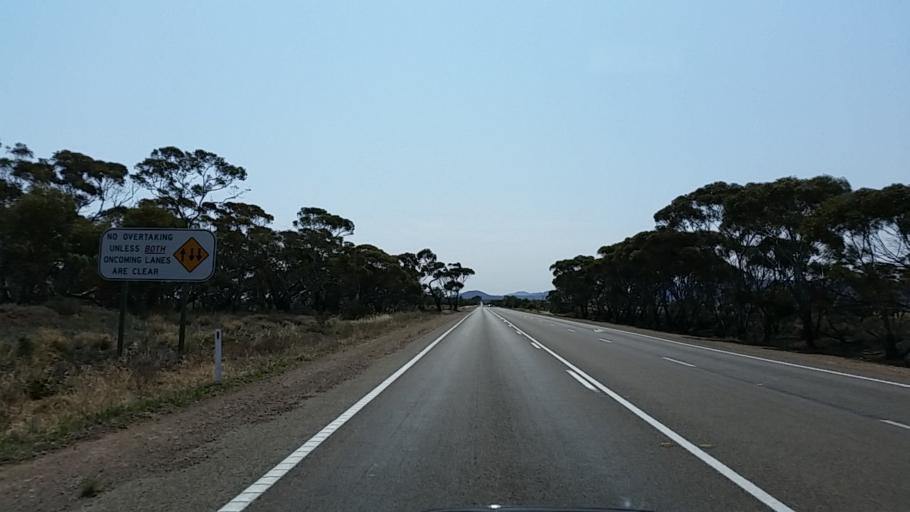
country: AU
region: South Australia
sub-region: Port Pirie City and Dists
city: Port Pirie
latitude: -32.9136
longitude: 137.9824
